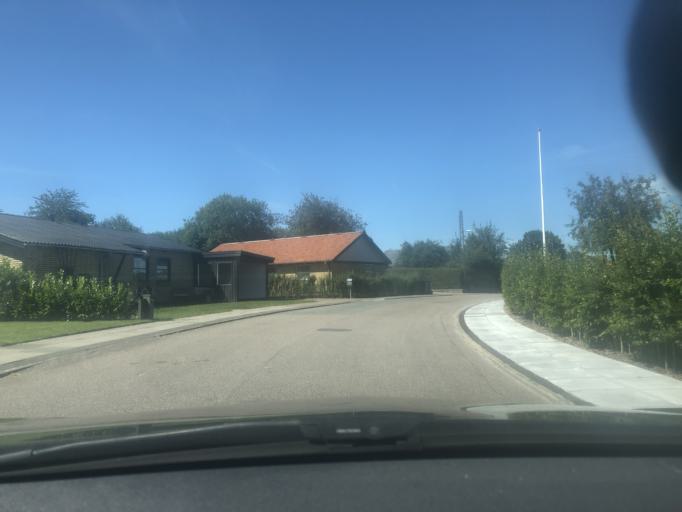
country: DK
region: South Denmark
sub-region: Vejle Kommune
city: Jelling
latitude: 55.6996
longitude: 9.3803
